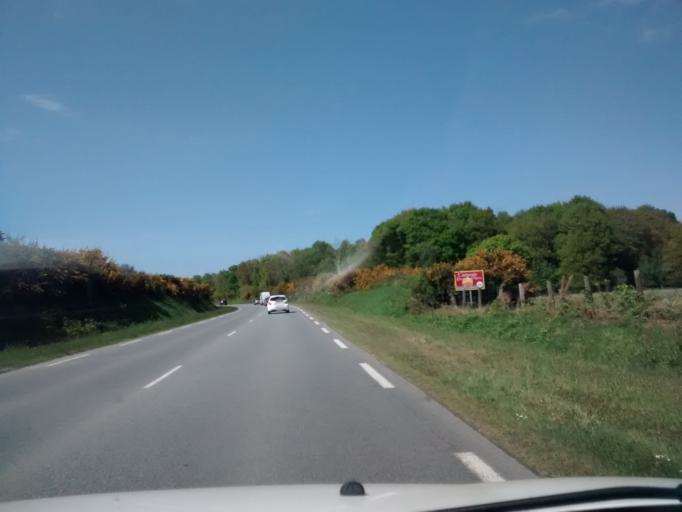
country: FR
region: Brittany
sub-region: Departement d'Ille-et-Vilaine
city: Pleurtuit
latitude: 48.5632
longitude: -2.0547
